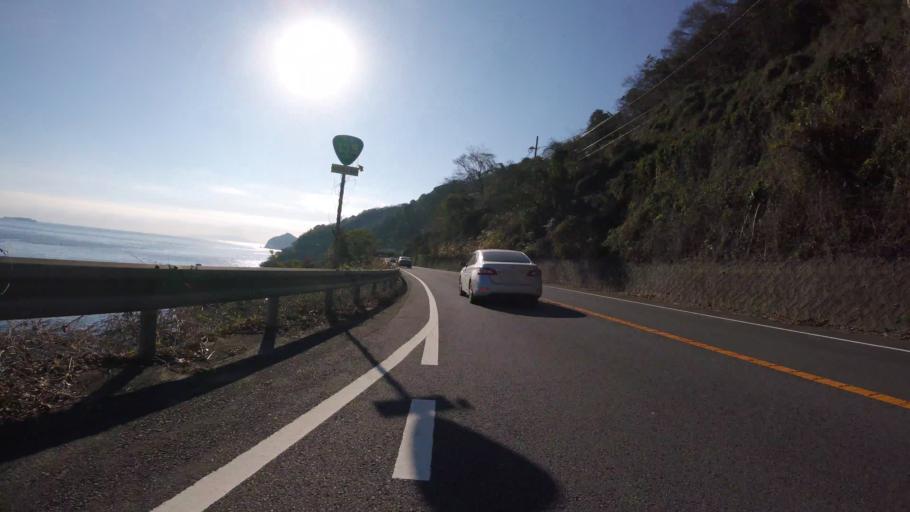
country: JP
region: Shizuoka
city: Atami
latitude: 35.0783
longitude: 139.0737
